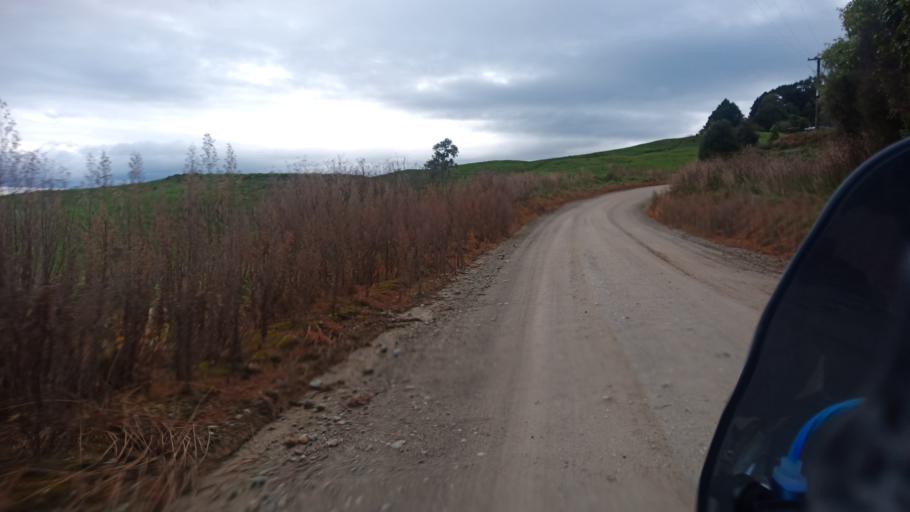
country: NZ
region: Gisborne
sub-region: Gisborne District
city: Gisborne
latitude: -38.3734
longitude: 177.9685
